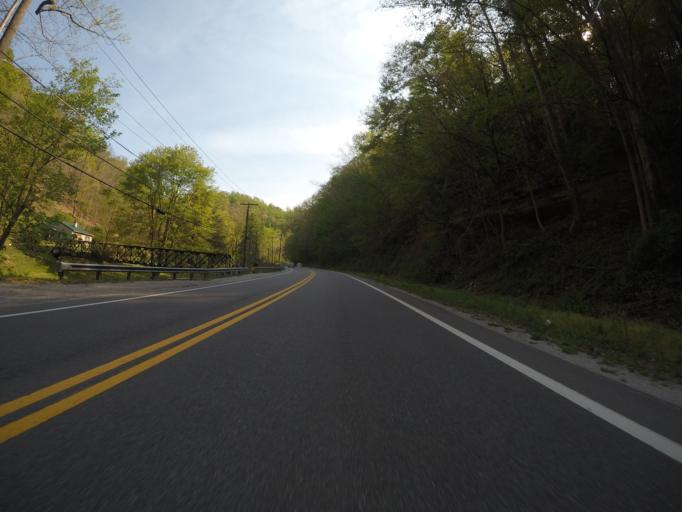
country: US
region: West Virginia
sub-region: Kanawha County
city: Charleston
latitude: 38.3635
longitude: -81.5849
